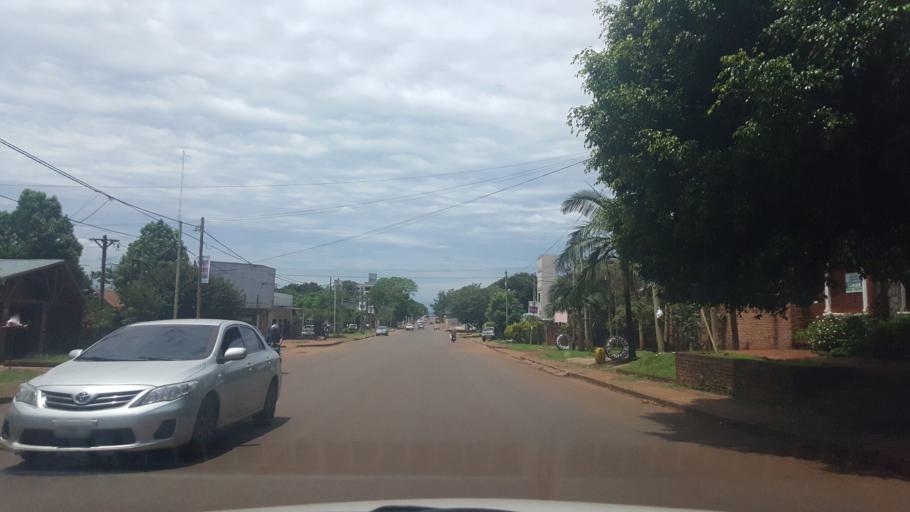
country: AR
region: Misiones
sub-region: Departamento de Capital
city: Posadas
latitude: -27.3786
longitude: -55.9215
